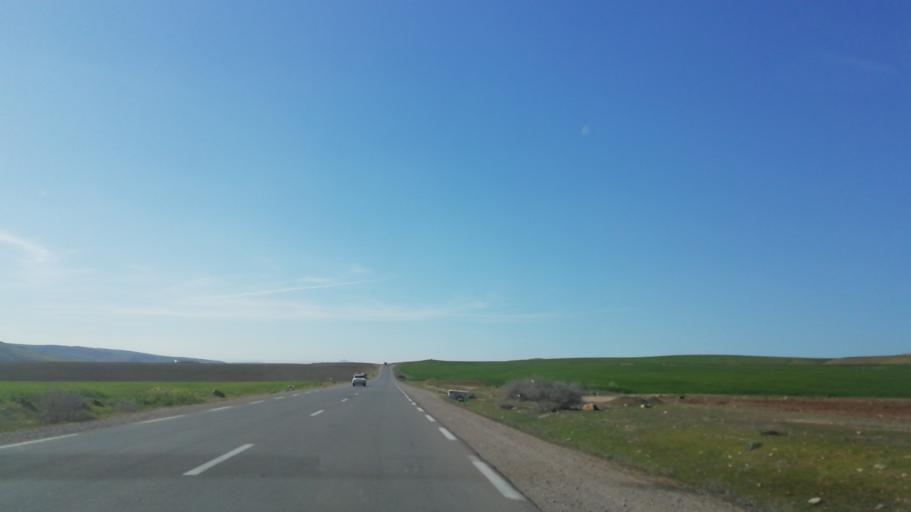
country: DZ
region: Mascara
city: Oued el Abtal
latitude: 35.4459
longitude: 0.8215
